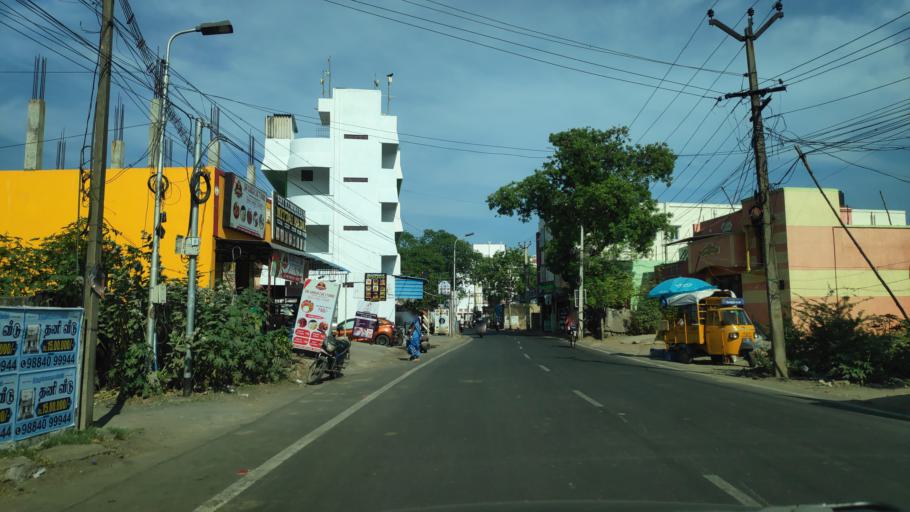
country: IN
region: Tamil Nadu
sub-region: Thiruvallur
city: Ambattur
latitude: 13.1173
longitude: 80.1700
